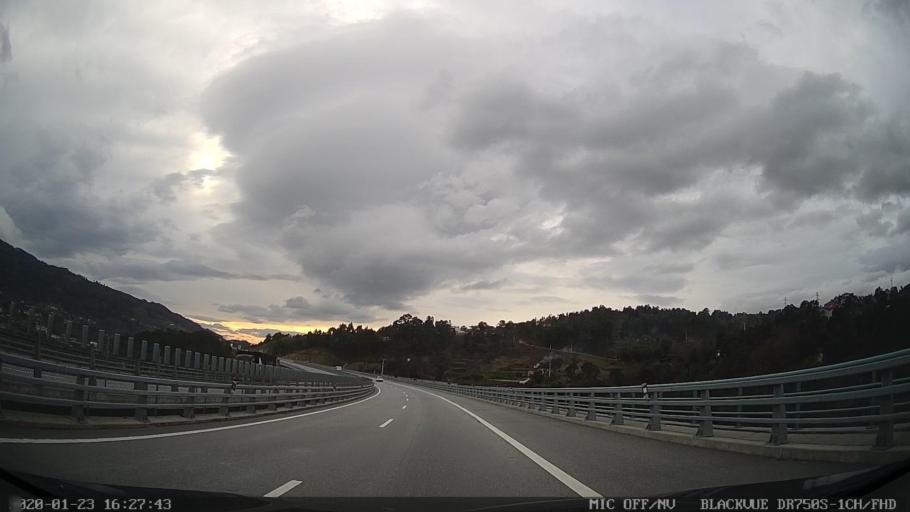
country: PT
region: Porto
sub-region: Amarante
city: Amarante
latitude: 41.2625
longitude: -8.0274
